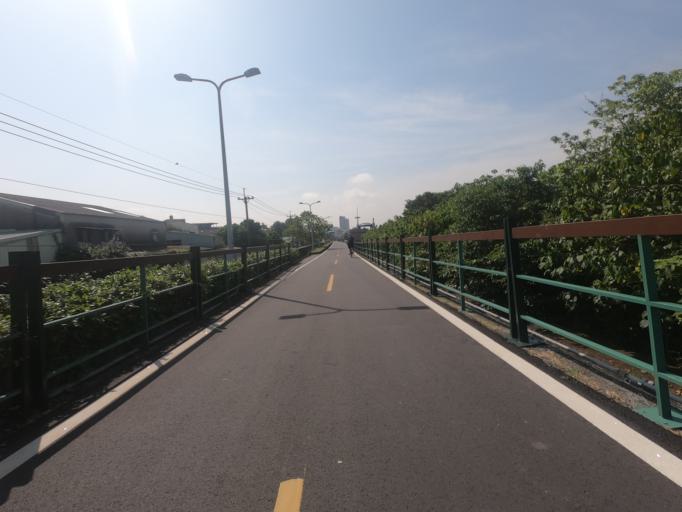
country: TW
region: Taipei
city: Taipei
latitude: 25.0983
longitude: 121.4915
